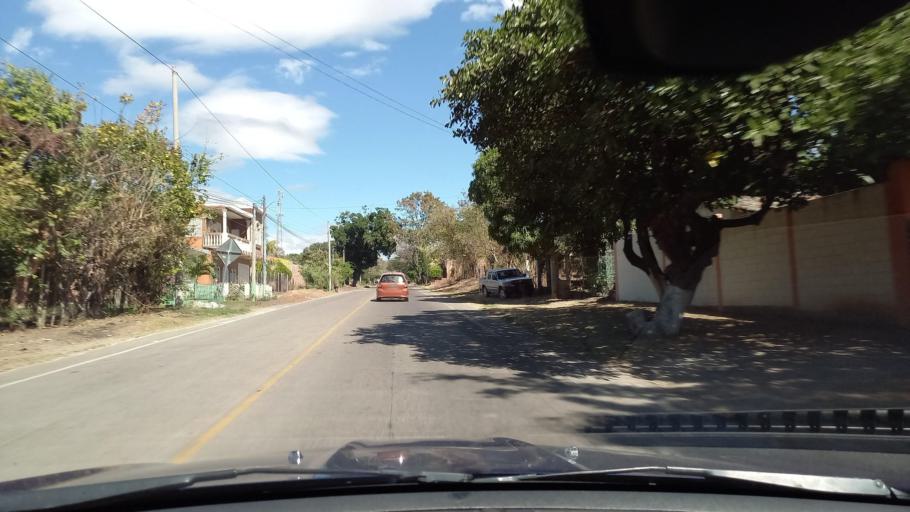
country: SV
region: Santa Ana
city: Metapan
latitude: 14.3534
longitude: -89.4540
